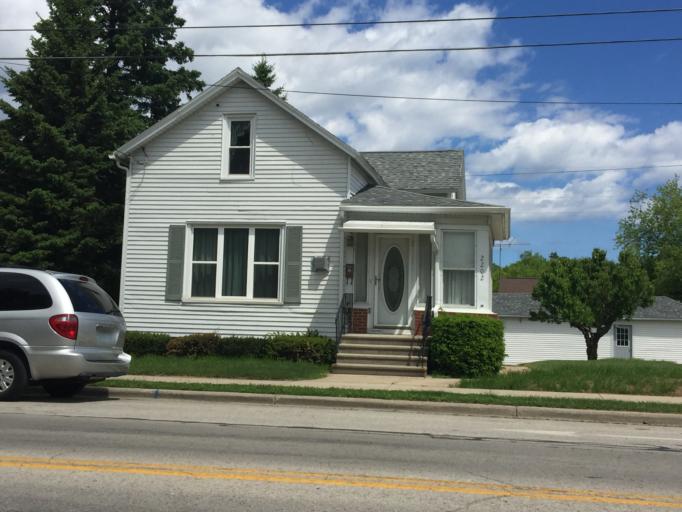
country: US
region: Michigan
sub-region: Menominee County
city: Menominee
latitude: 45.1190
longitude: -87.6185
